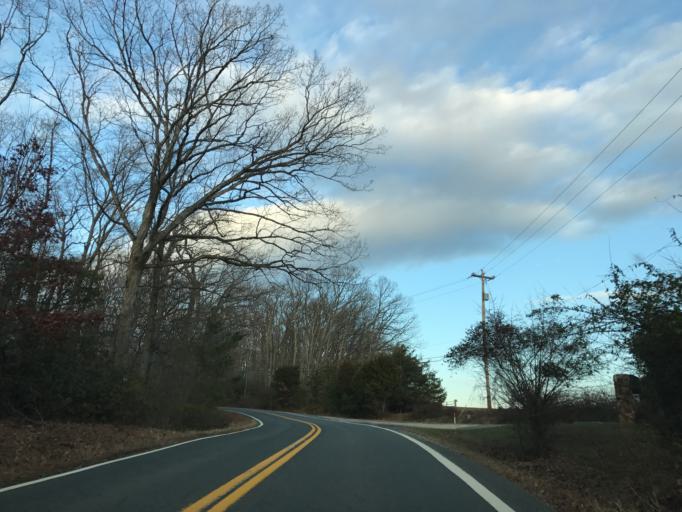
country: US
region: Maryland
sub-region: Cecil County
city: Charlestown
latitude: 39.5028
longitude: -75.9610
